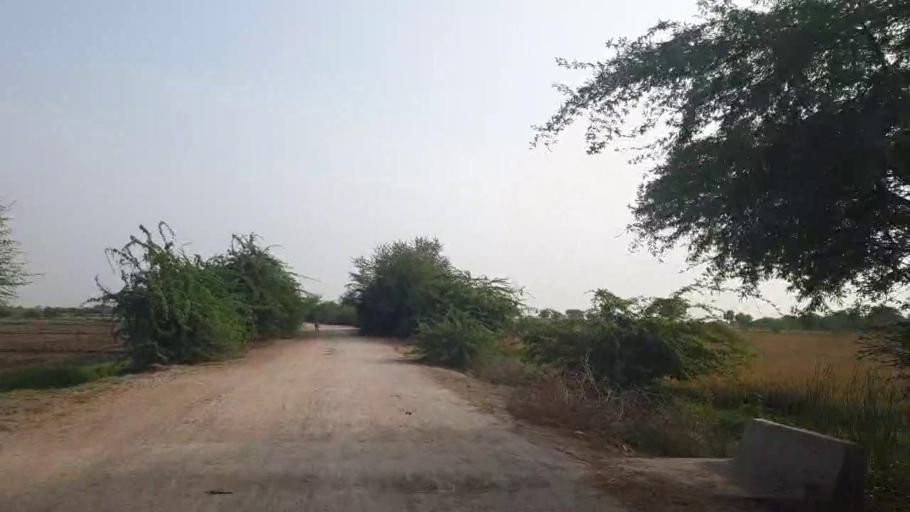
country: PK
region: Sindh
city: Badin
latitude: 24.6088
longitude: 68.6877
